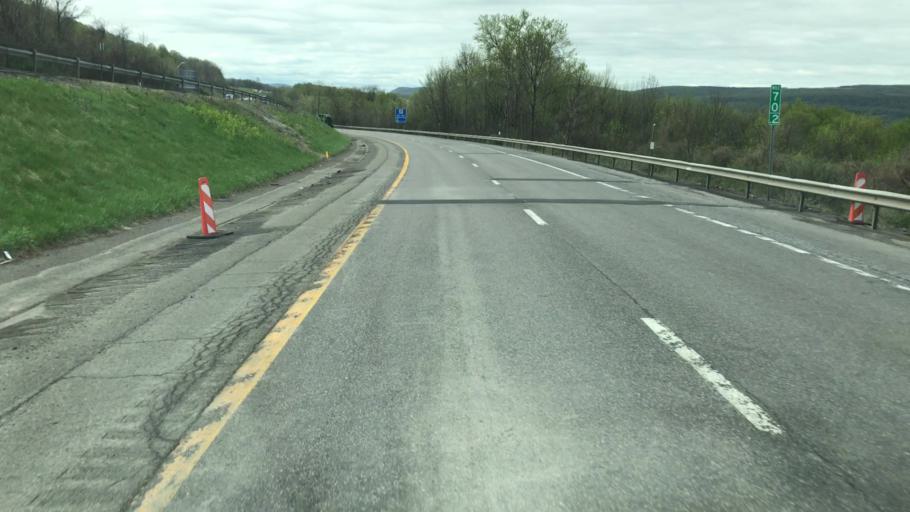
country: US
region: New York
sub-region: Onondaga County
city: Nedrow
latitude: 42.8425
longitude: -76.1231
